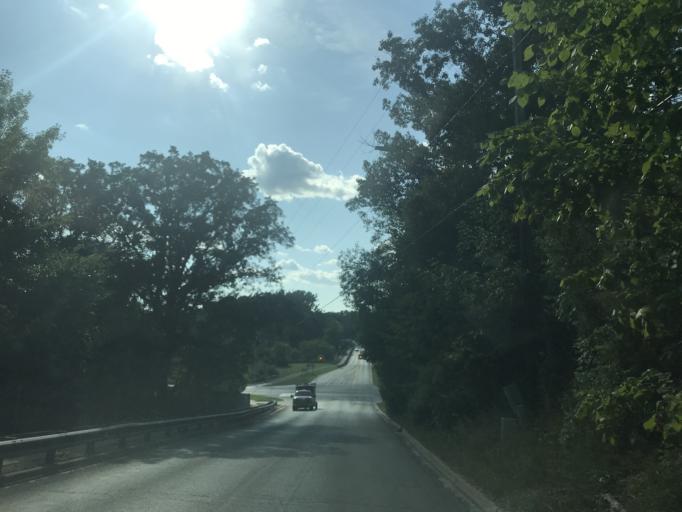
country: US
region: Michigan
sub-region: Newaygo County
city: Newaygo
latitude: 43.4237
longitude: -85.7962
